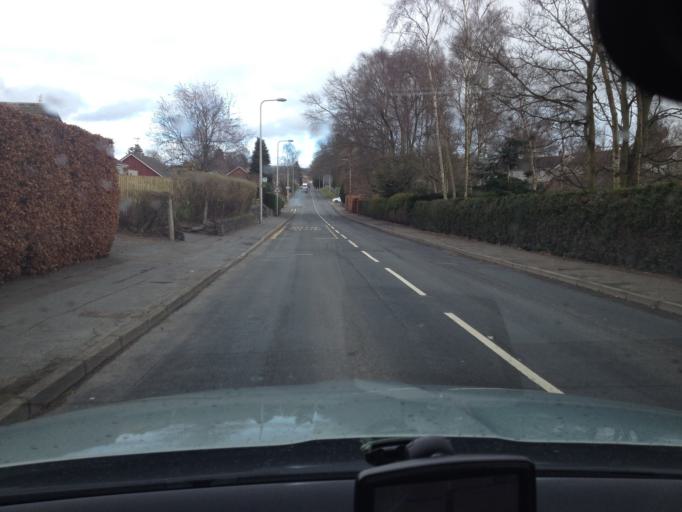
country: GB
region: Scotland
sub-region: Perth and Kinross
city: Scone
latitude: 56.4232
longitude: -3.4091
